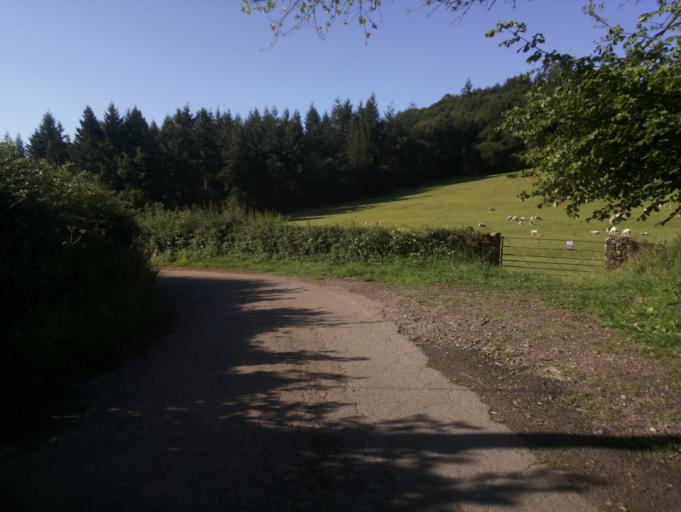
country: GB
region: England
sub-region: Gloucestershire
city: Coleford
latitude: 51.7888
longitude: -2.6370
